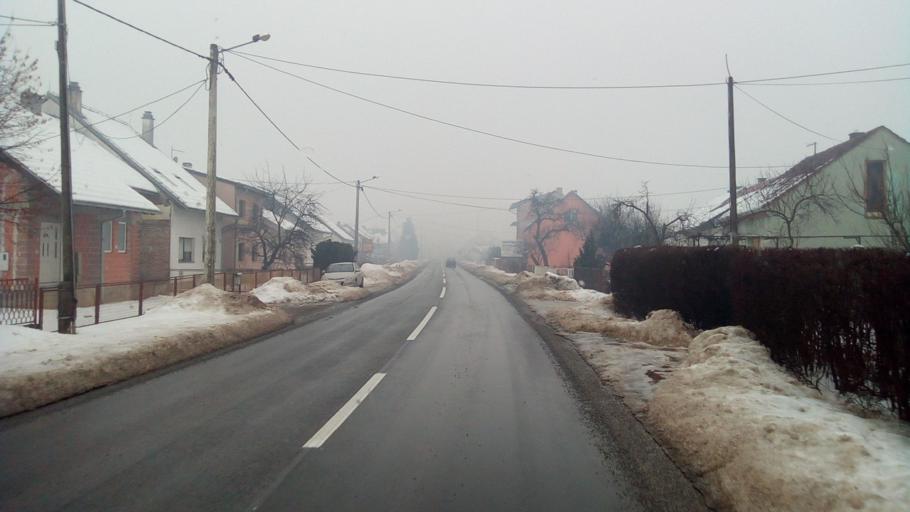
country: HR
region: Sisacko-Moslavacka
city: Petrinja
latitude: 45.4268
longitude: 16.2829
